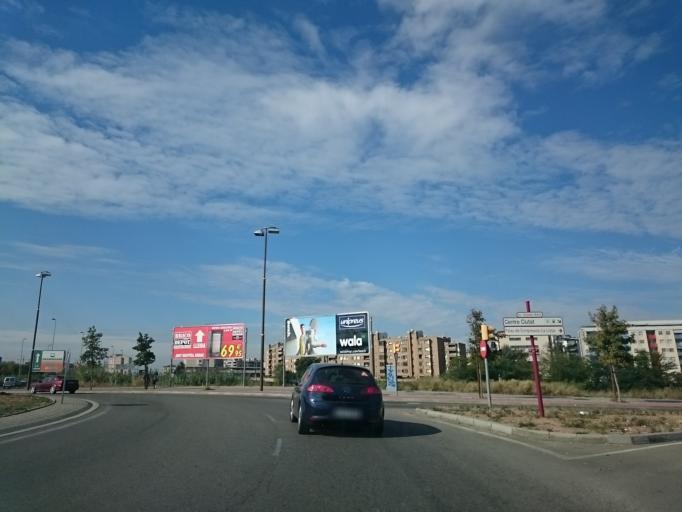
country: ES
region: Catalonia
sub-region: Provincia de Lleida
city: Lleida
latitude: 41.6107
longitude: 0.6402
